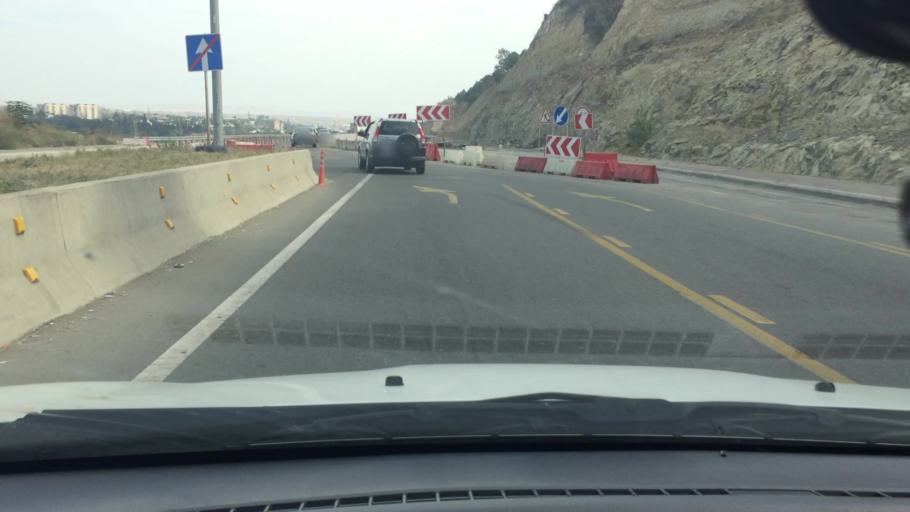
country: GE
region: T'bilisi
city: Tbilisi
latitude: 41.6627
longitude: 44.8770
